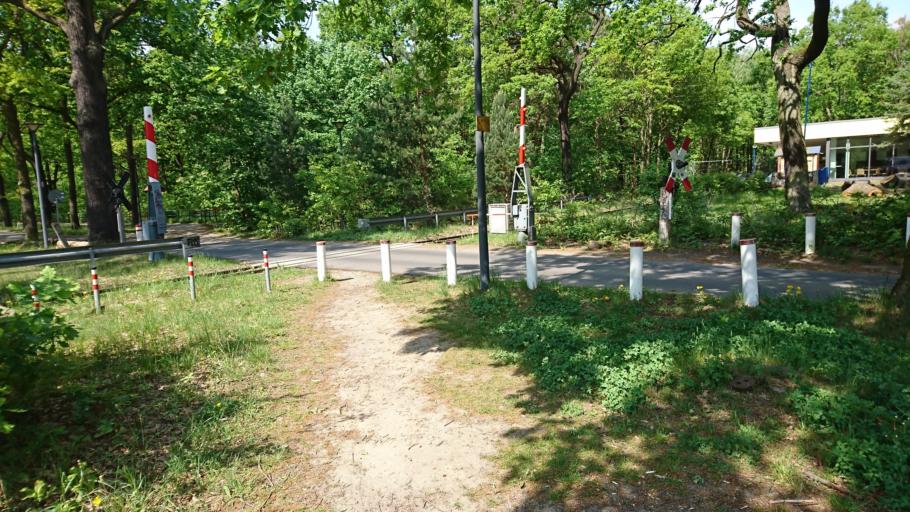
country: DE
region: Berlin
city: Adlershof
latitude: 52.4592
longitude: 13.5527
